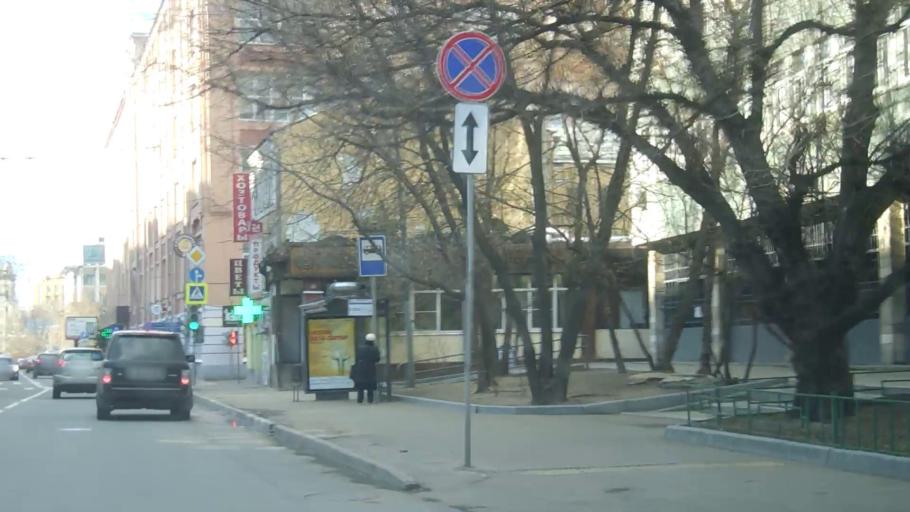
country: RU
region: Moscow
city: Moscow
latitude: 55.7760
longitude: 37.6075
